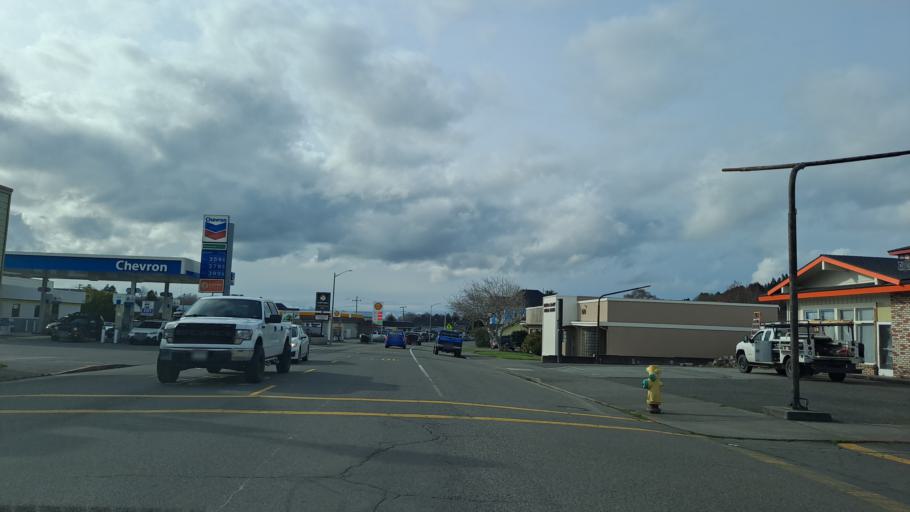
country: US
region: California
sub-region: Humboldt County
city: Fortuna
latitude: 40.5980
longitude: -124.1576
